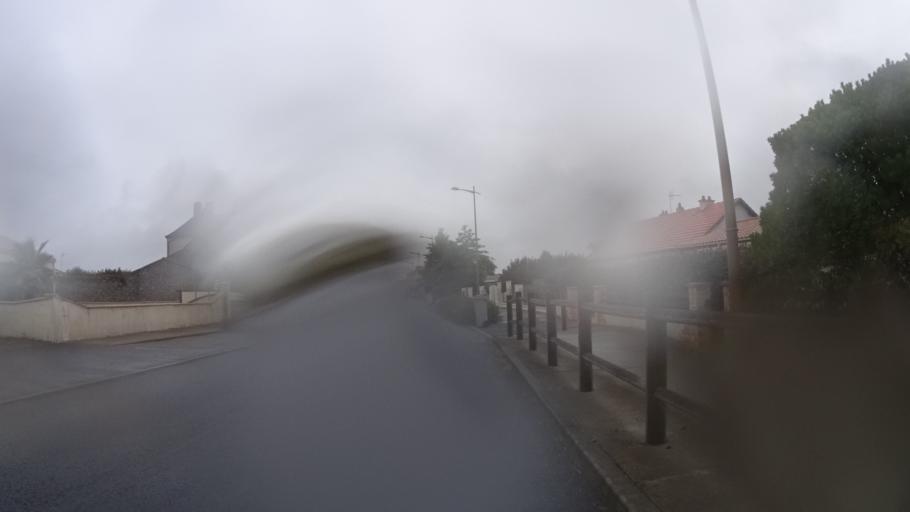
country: FR
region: Pays de la Loire
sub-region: Departement de la Loire-Atlantique
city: Corsept
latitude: 47.2754
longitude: -2.0608
